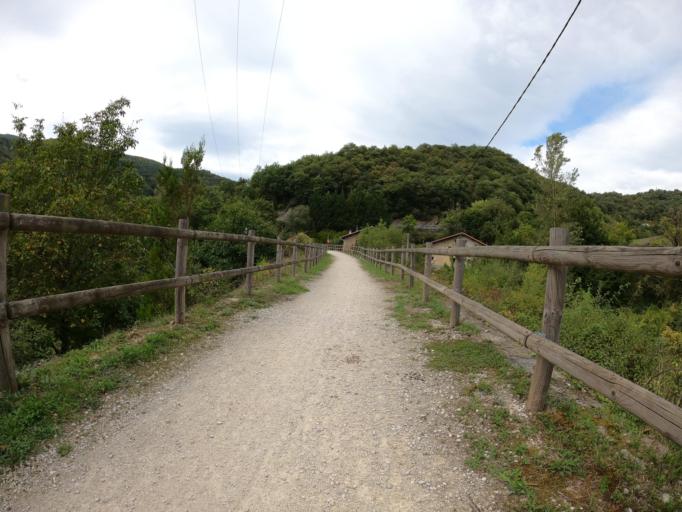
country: ES
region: Navarre
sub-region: Provincia de Navarra
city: Irurtzun
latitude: 42.9625
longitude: -1.8270
